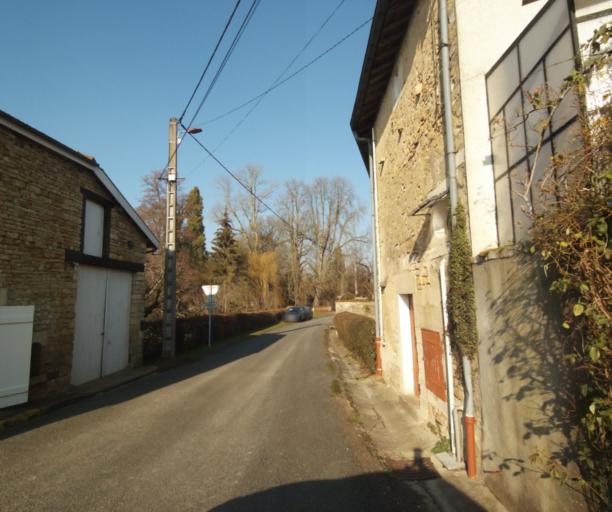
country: FR
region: Champagne-Ardenne
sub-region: Departement de la Haute-Marne
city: Wassy
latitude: 48.4474
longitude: 4.9566
